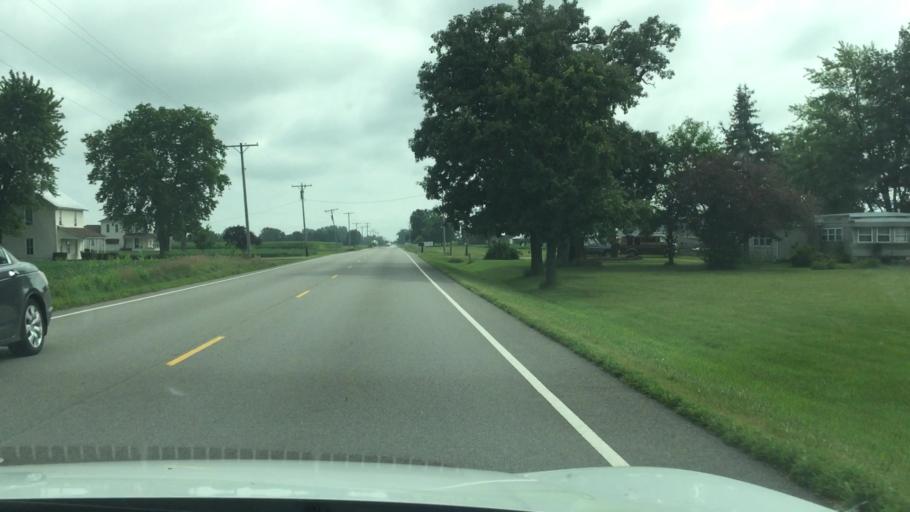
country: US
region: Ohio
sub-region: Union County
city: Marysville
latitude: 40.1684
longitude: -83.4441
